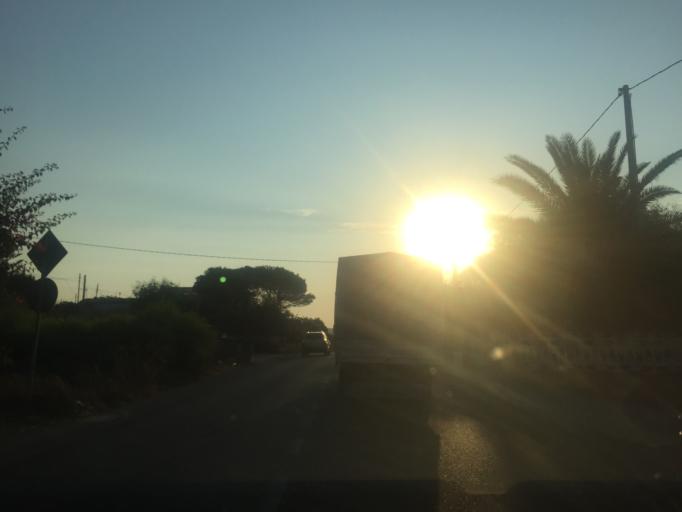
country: IT
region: Sicily
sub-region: Ragusa
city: Cava d'Aliga
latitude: 36.7199
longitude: 14.7092
